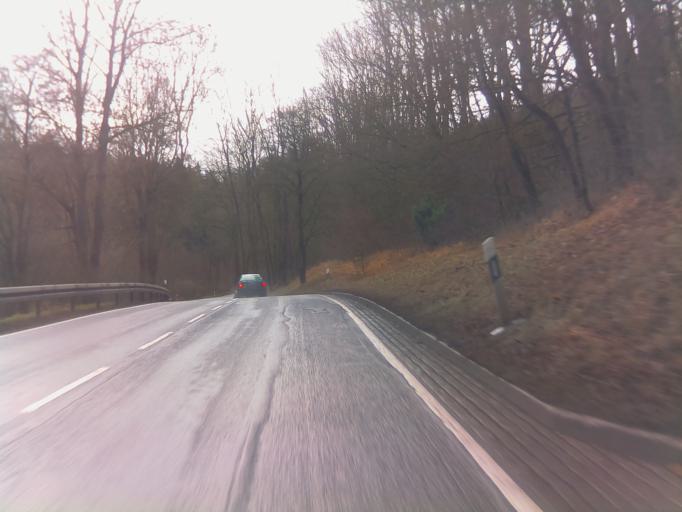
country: DE
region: Thuringia
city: Rippershausen
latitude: 50.5637
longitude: 10.3426
